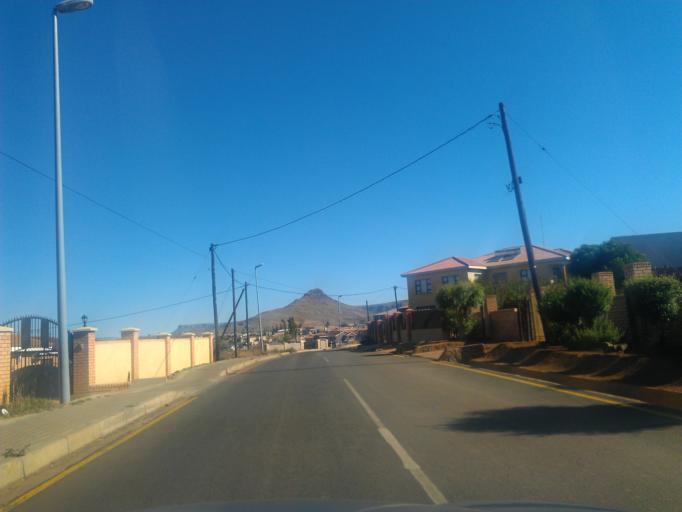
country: LS
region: Maseru
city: Maseru
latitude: -29.3435
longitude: 27.4478
